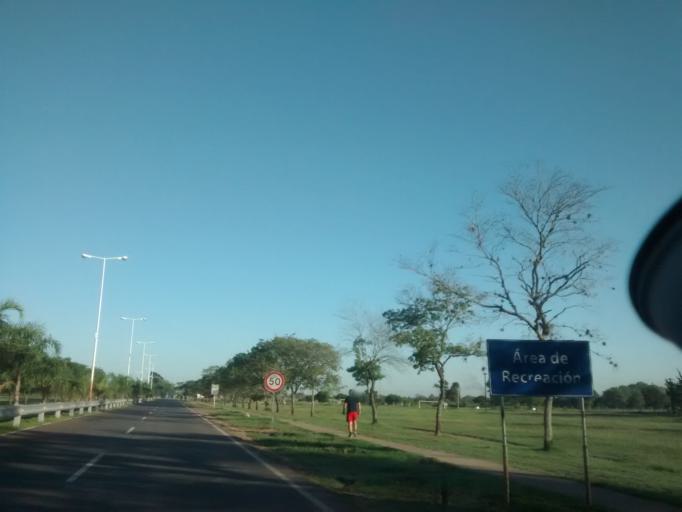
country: AR
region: Chaco
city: Fontana
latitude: -27.4432
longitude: -59.0259
